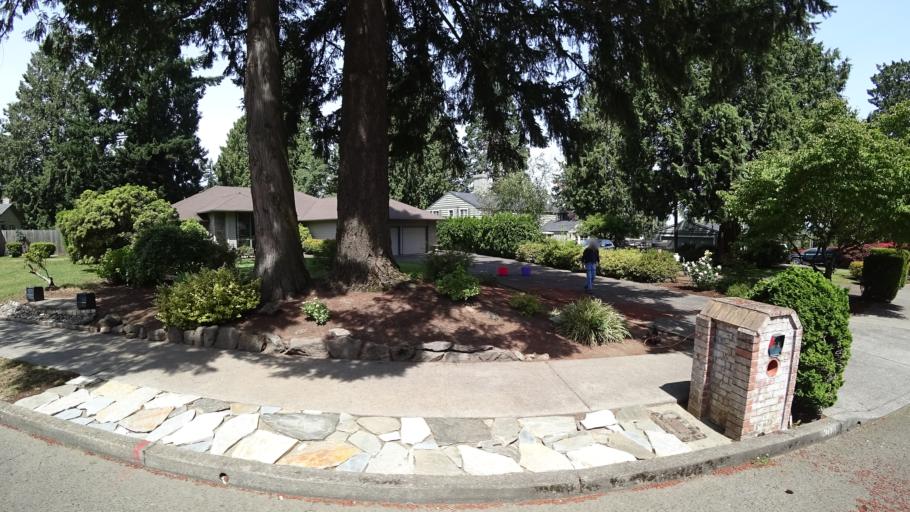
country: US
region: Oregon
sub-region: Multnomah County
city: Fairview
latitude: 45.5447
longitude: -122.5019
